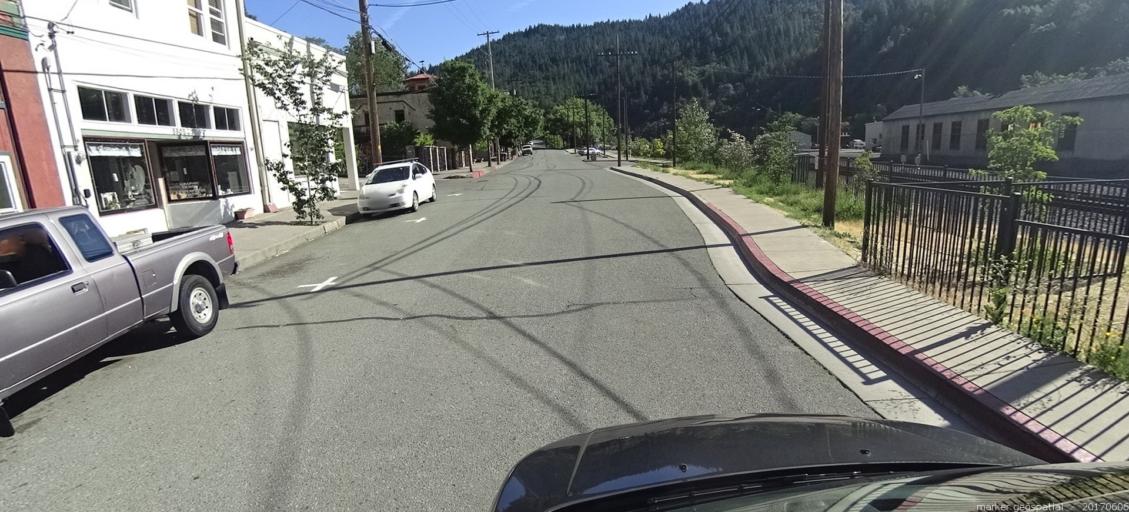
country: US
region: California
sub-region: Siskiyou County
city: Dunsmuir
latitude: 41.2091
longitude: -122.2718
